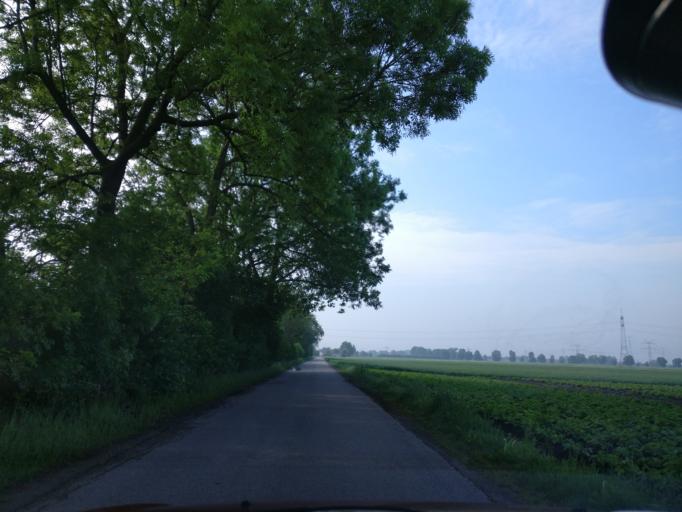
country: DE
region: Bavaria
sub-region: Upper Bavaria
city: Karlsfeld
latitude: 48.2185
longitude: 11.4423
